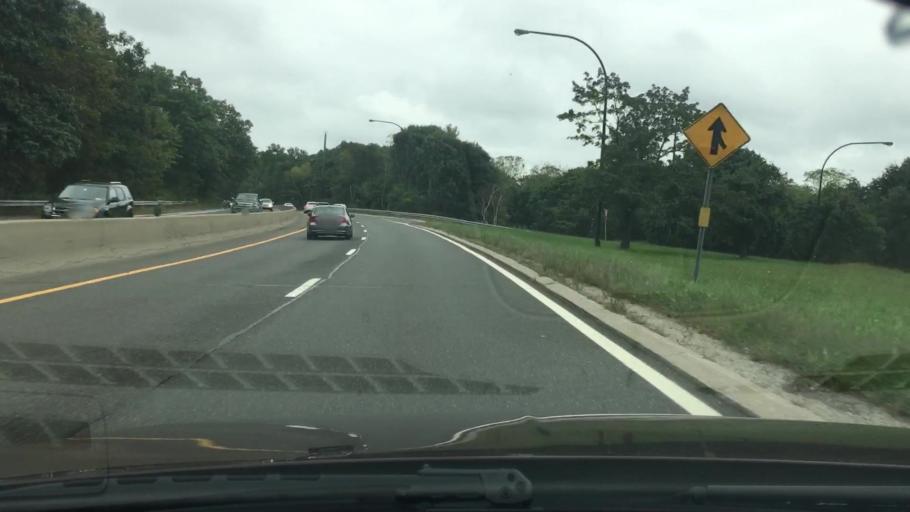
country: US
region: New York
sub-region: Suffolk County
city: West Hills
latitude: 40.8024
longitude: -73.4434
